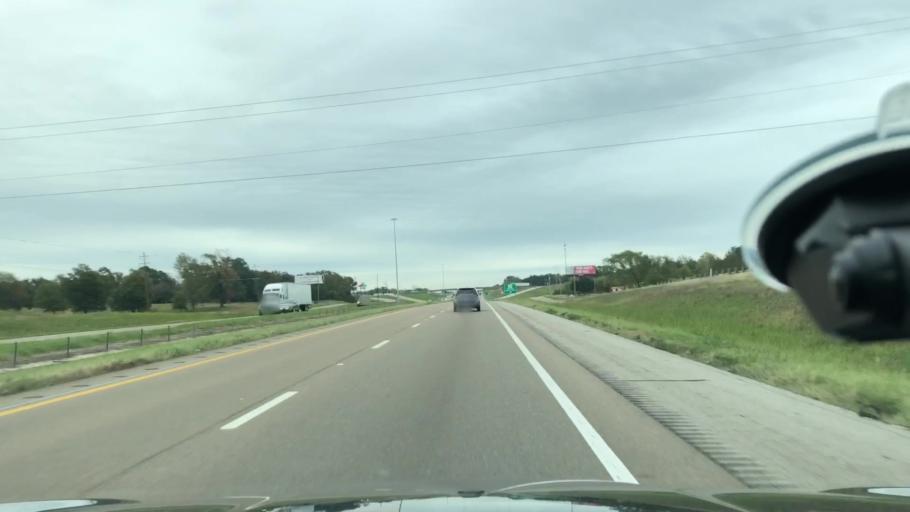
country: US
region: Texas
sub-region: Franklin County
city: Mount Vernon
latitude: 33.1606
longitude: -95.1223
